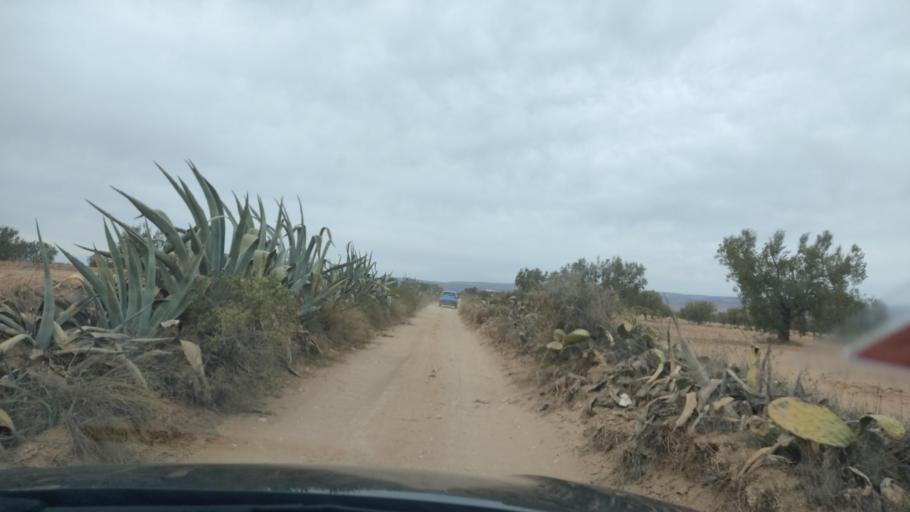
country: TN
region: Al Qasrayn
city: Kasserine
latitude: 35.2242
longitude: 8.9375
